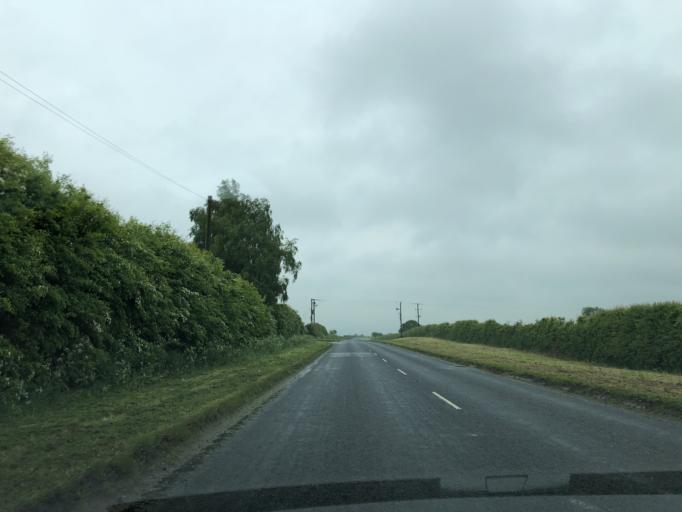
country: GB
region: England
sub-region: North Yorkshire
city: Thirsk
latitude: 54.2182
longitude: -1.4215
